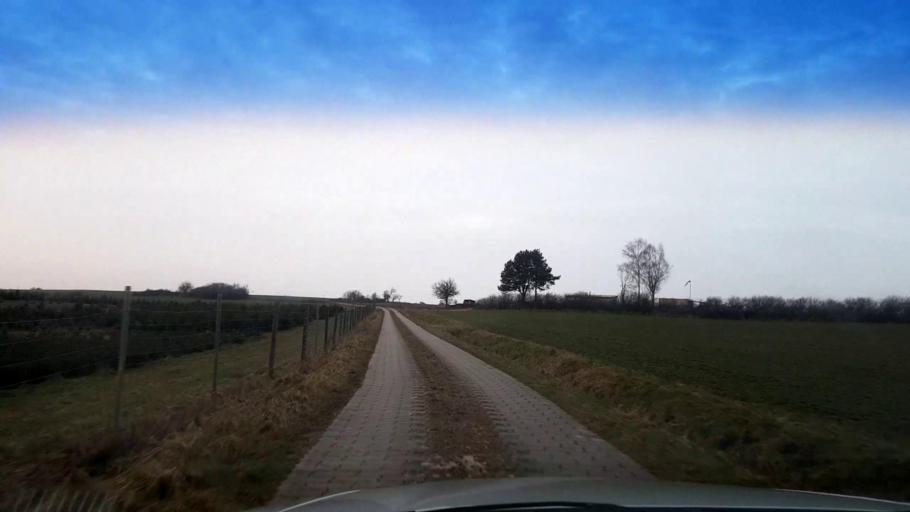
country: DE
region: Bavaria
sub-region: Upper Franconia
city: Pommersfelden
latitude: 49.8066
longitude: 10.8246
